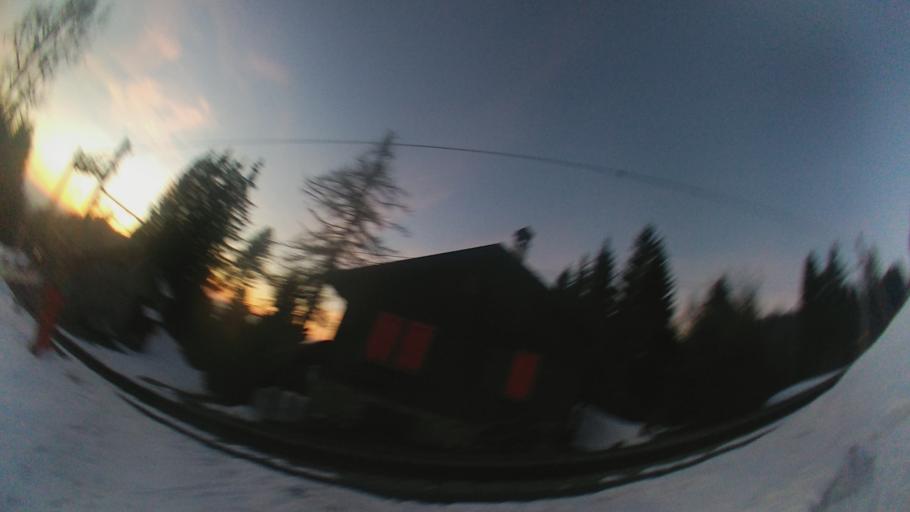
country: CH
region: Vaud
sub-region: Riviera-Pays-d'Enhaut District
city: Caux
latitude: 46.4351
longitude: 6.9563
